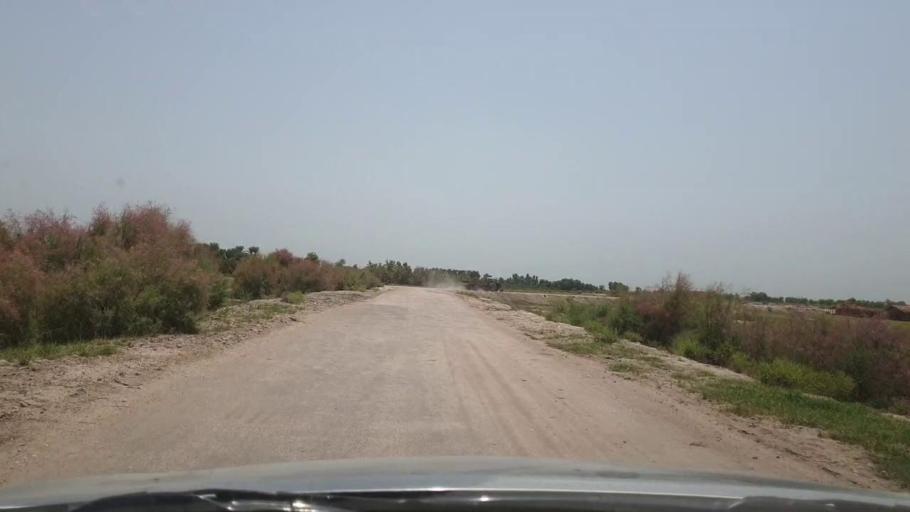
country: PK
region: Sindh
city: Pano Aqil
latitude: 27.8710
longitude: 69.1676
